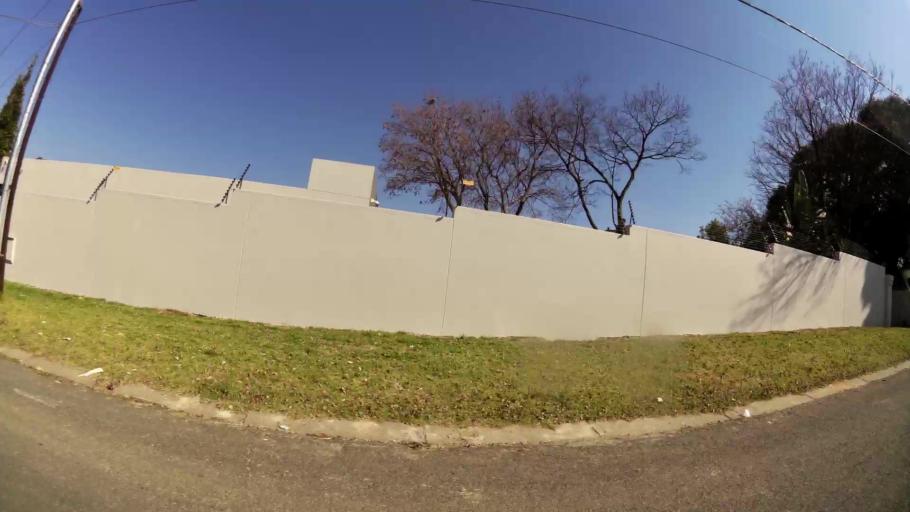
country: ZA
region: Gauteng
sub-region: City of Johannesburg Metropolitan Municipality
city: Modderfontein
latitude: -26.1437
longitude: 28.1044
